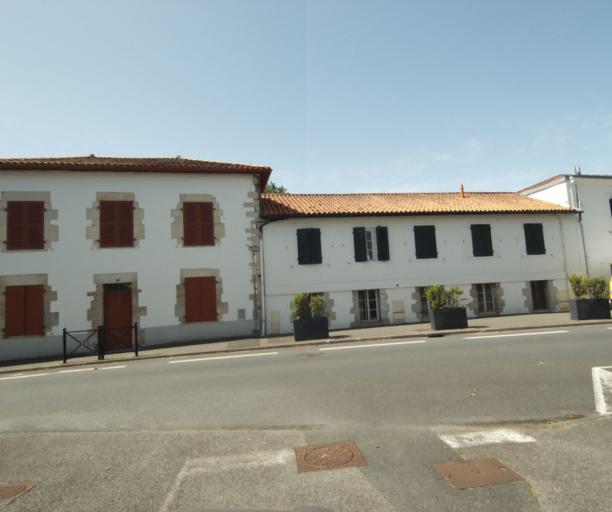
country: FR
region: Aquitaine
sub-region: Departement des Pyrenees-Atlantiques
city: Bayonne
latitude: 43.4796
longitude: -1.4594
